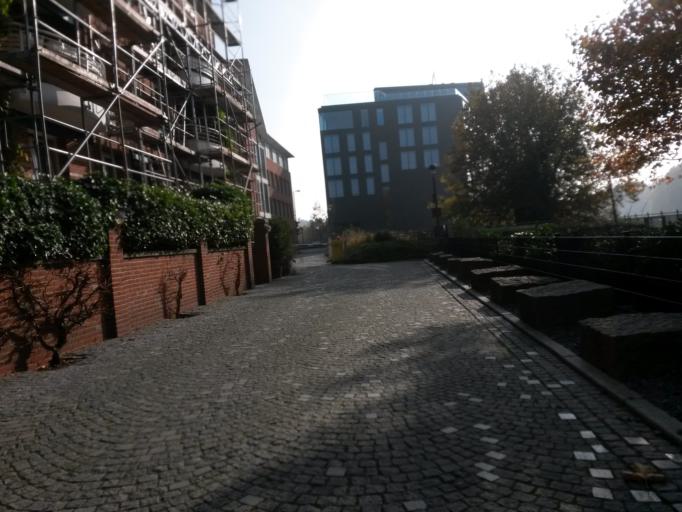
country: DE
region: Bremen
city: Bremen
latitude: 53.0746
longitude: 8.8014
